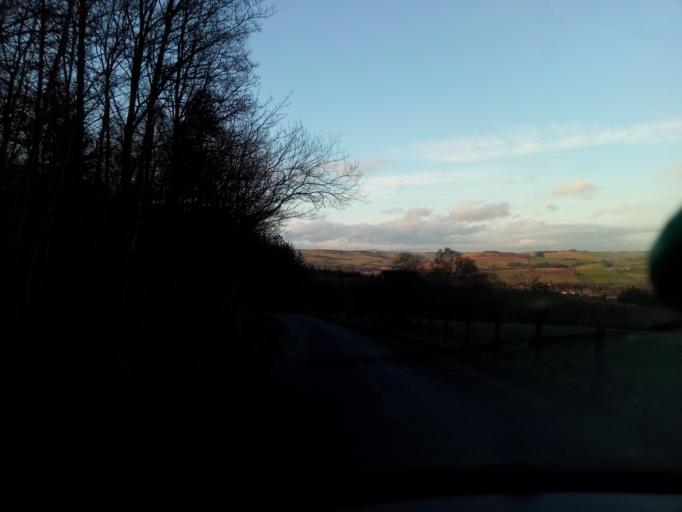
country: GB
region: Scotland
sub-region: The Scottish Borders
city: Melrose
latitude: 55.5822
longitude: -2.7390
